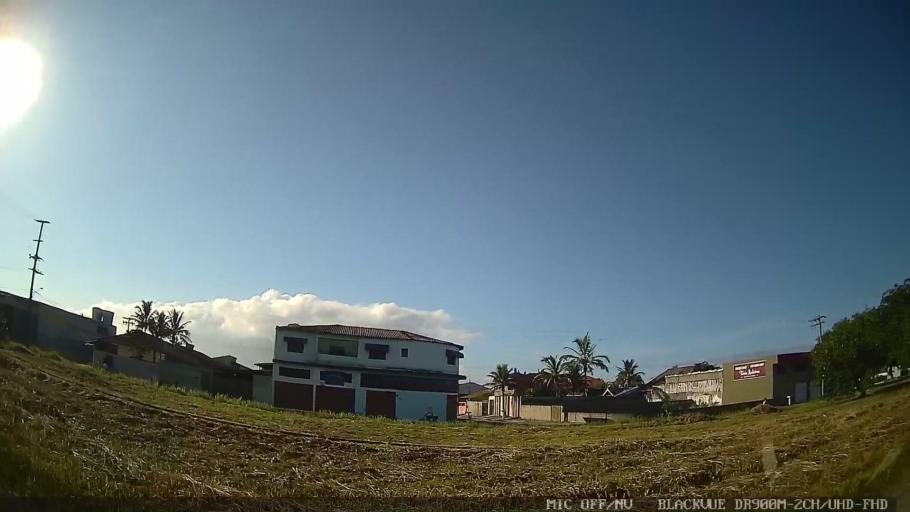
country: BR
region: Sao Paulo
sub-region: Peruibe
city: Peruibe
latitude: -24.2755
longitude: -46.9529
